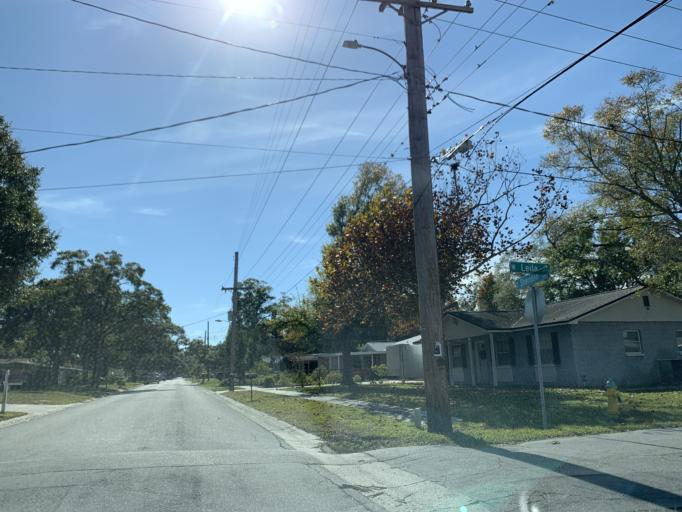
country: US
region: Florida
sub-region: Hillsborough County
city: Tampa
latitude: 27.8845
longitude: -82.4981
